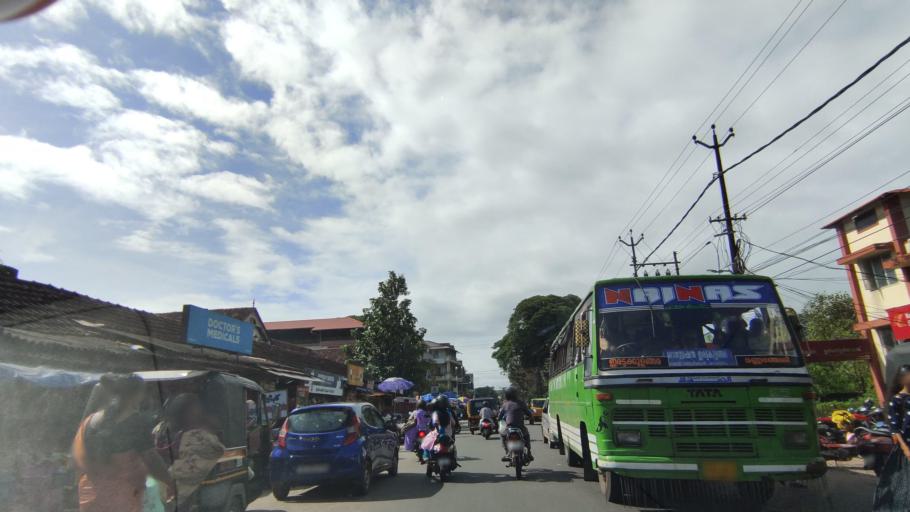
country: IN
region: Kerala
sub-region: Alappuzha
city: Alleppey
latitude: 9.5016
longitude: 76.3418
